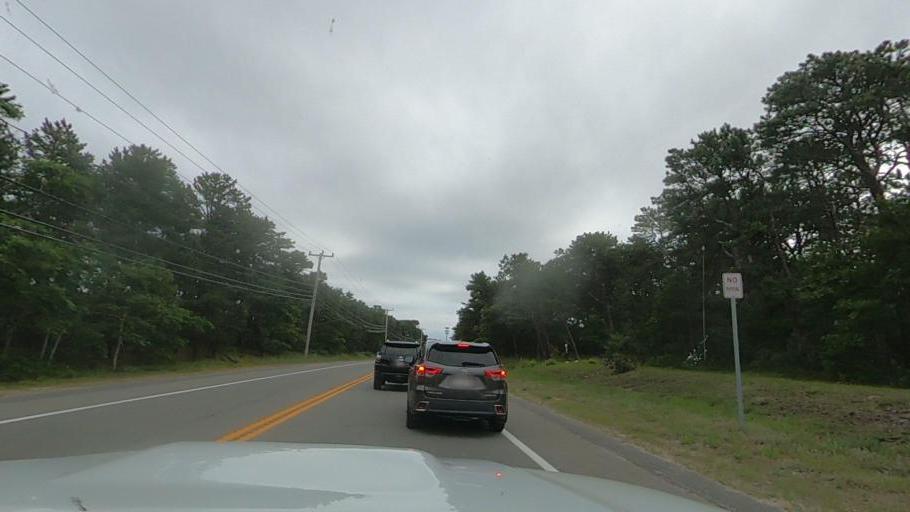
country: US
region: Massachusetts
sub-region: Barnstable County
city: North Eastham
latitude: 41.9029
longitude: -69.9846
